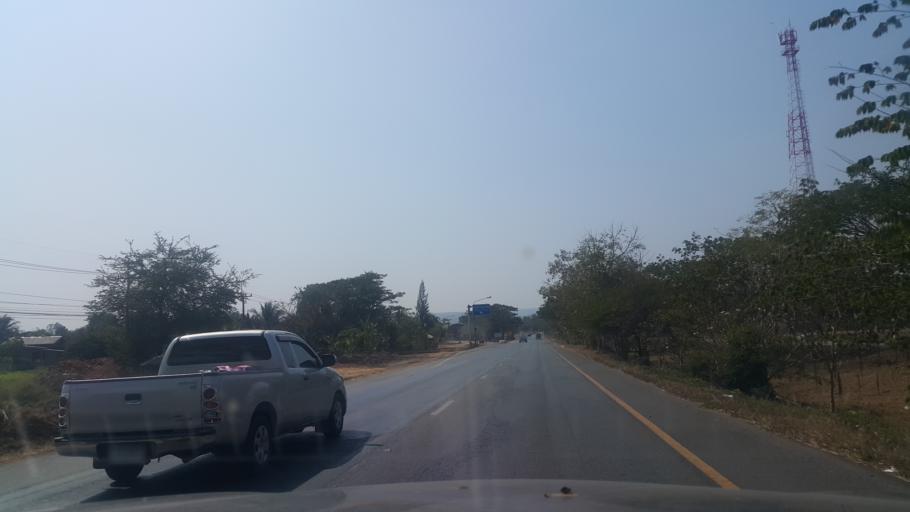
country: TH
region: Nakhon Ratchasima
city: Wang Nam Khiao
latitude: 14.5330
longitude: 101.9669
